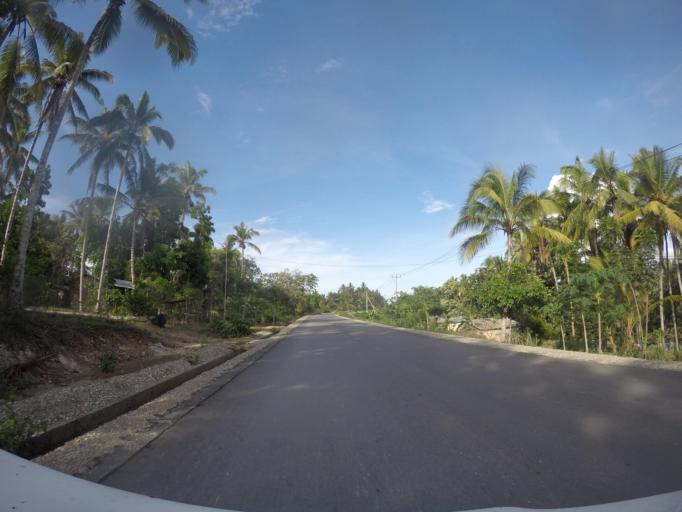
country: TL
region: Baucau
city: Baucau
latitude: -8.5032
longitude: 126.4469
